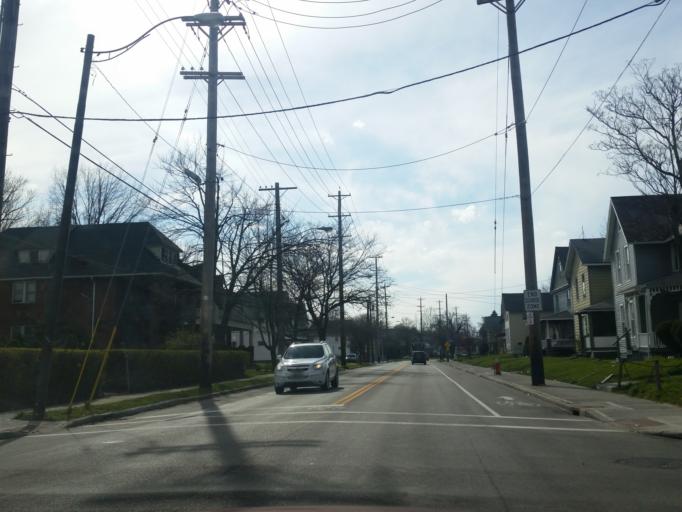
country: US
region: Ohio
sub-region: Cuyahoga County
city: Brooklyn Heights
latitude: 41.4507
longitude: -81.7050
